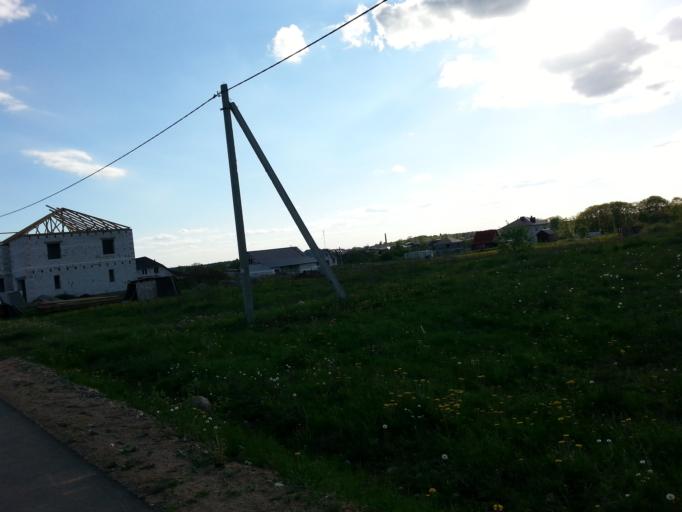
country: BY
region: Minsk
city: Narach
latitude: 54.9383
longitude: 26.6993
